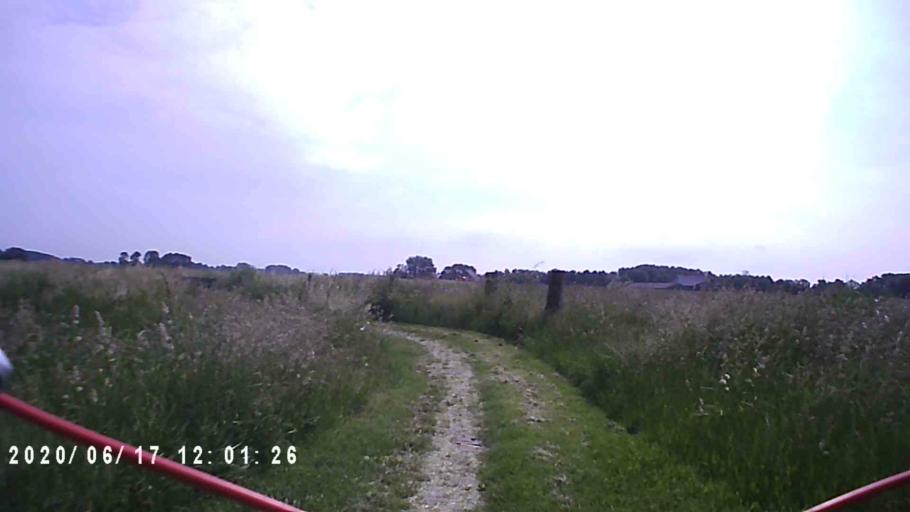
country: NL
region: Groningen
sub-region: Gemeente De Marne
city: Ulrum
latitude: 53.3411
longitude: 6.3356
